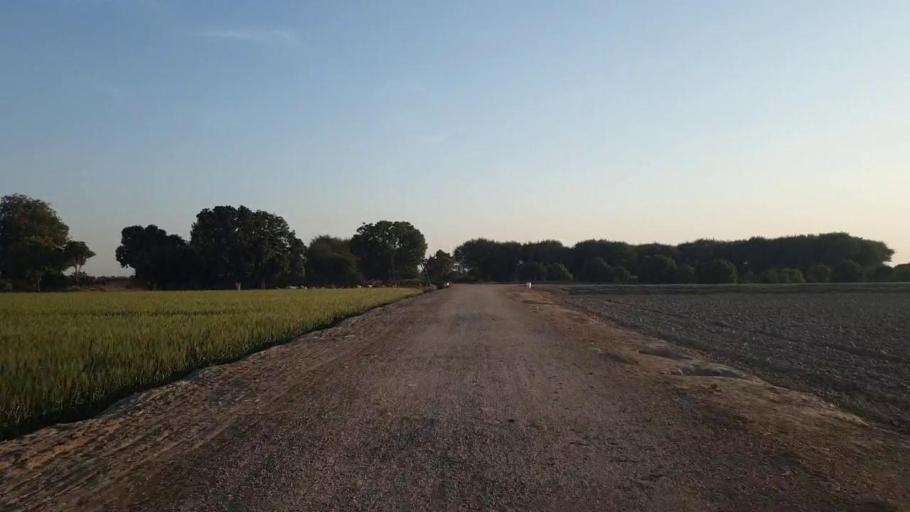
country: PK
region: Sindh
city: Chambar
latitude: 25.2633
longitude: 68.7656
